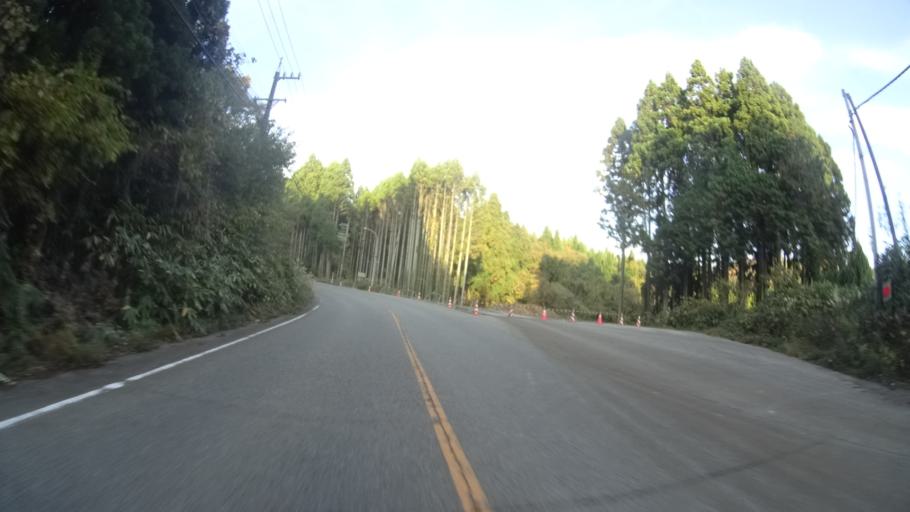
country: JP
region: Ishikawa
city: Nanao
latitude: 37.1808
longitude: 136.7139
